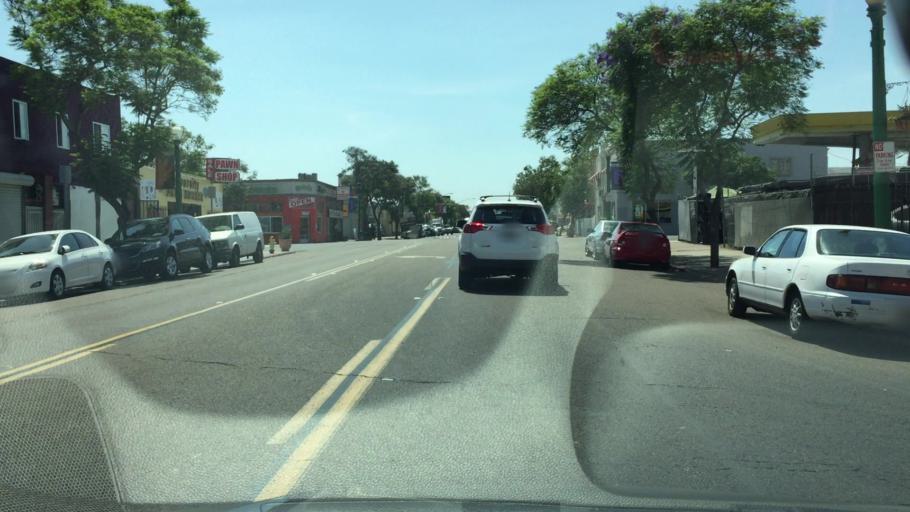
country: US
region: California
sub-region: San Diego County
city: San Diego
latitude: 32.7498
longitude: -117.1137
